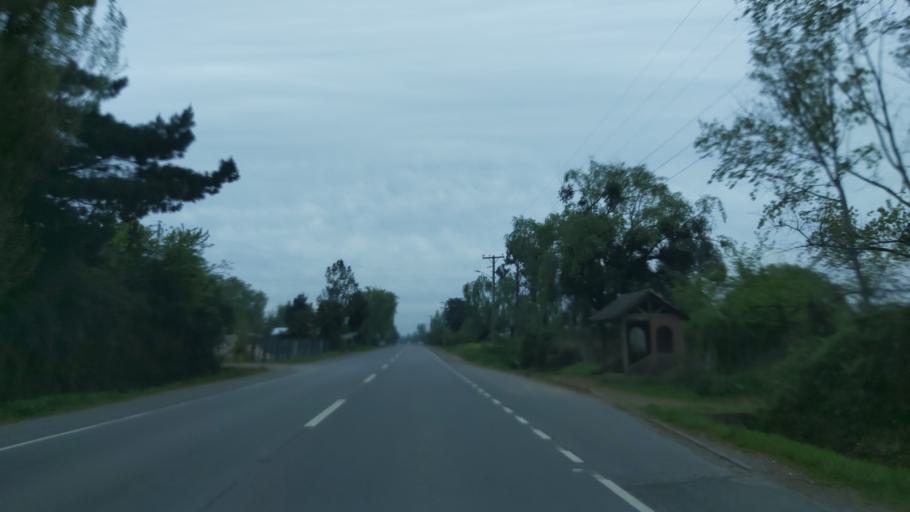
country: CL
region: Maule
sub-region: Provincia de Linares
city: Linares
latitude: -35.7683
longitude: -71.5138
